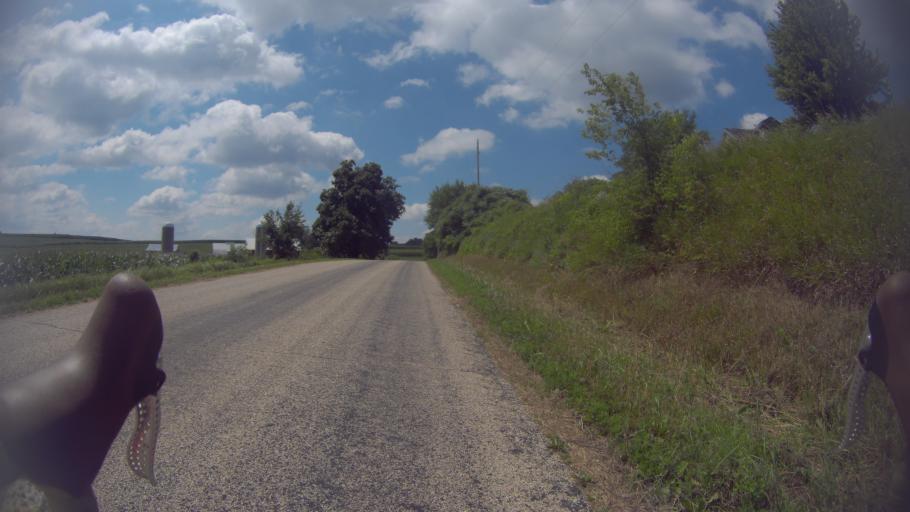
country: US
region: Wisconsin
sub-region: Sauk County
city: Sauk City
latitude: 43.2357
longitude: -89.6396
